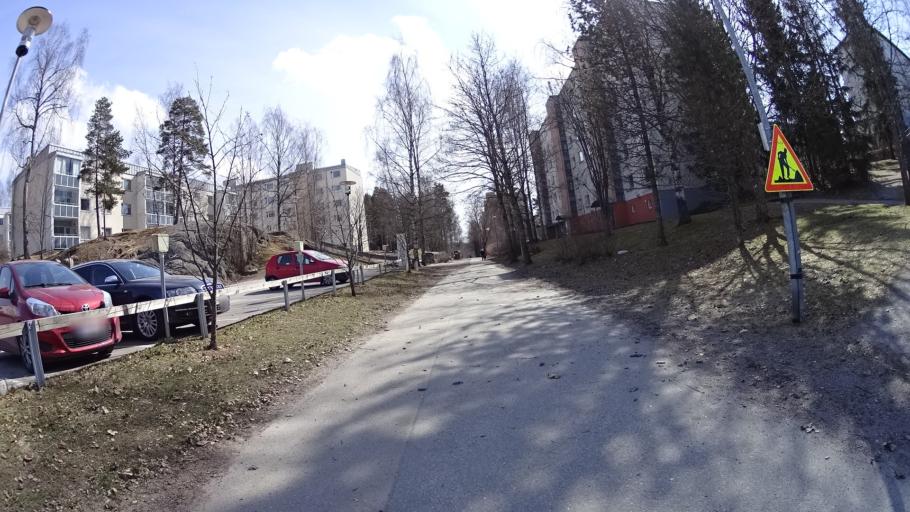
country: FI
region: Uusimaa
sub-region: Helsinki
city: Kilo
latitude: 60.2788
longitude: 24.8401
